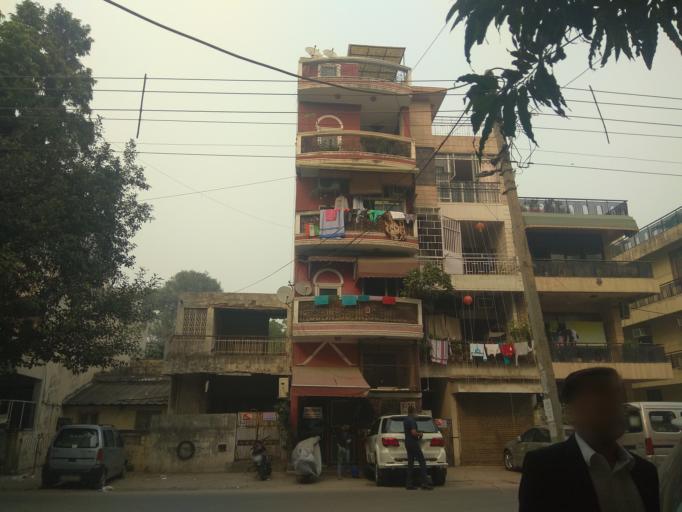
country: IN
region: NCT
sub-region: New Delhi
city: New Delhi
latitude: 28.5728
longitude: 77.2447
